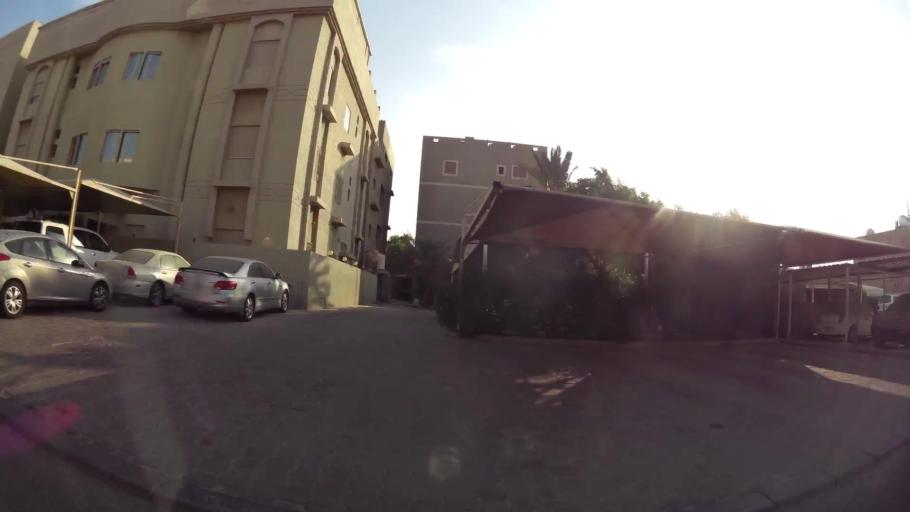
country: KW
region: Muhafazat Hawalli
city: As Salimiyah
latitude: 29.3231
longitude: 48.0722
